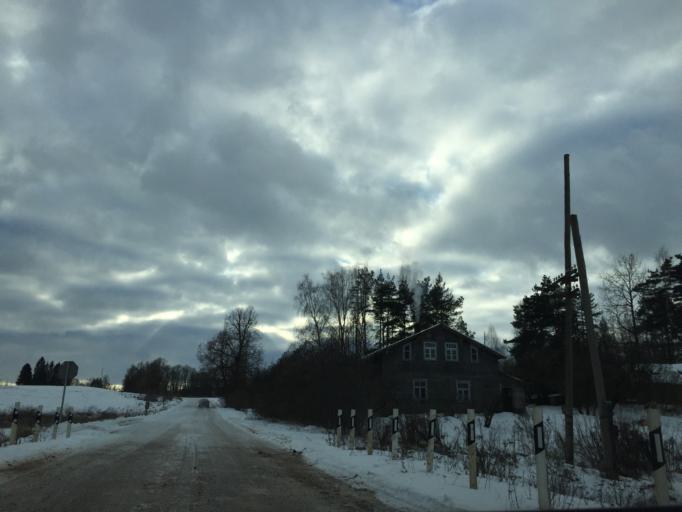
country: LV
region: Lielvarde
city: Lielvarde
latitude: 56.5812
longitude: 24.7350
